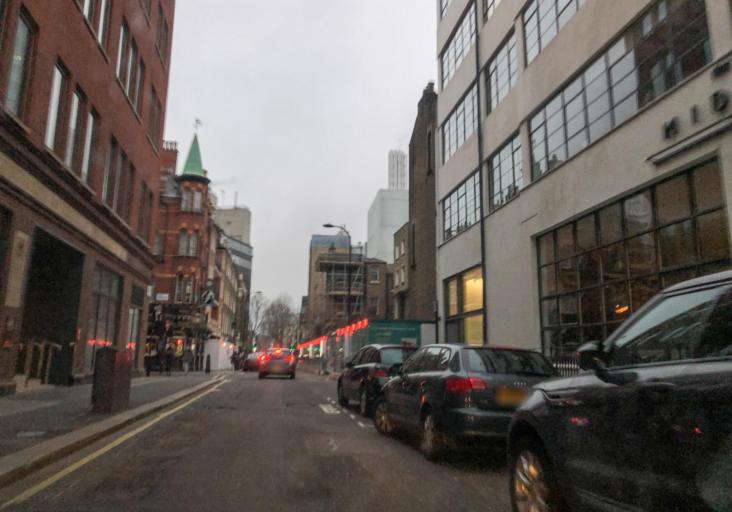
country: GB
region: England
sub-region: Greater London
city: London
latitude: 51.5199
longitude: -0.1379
